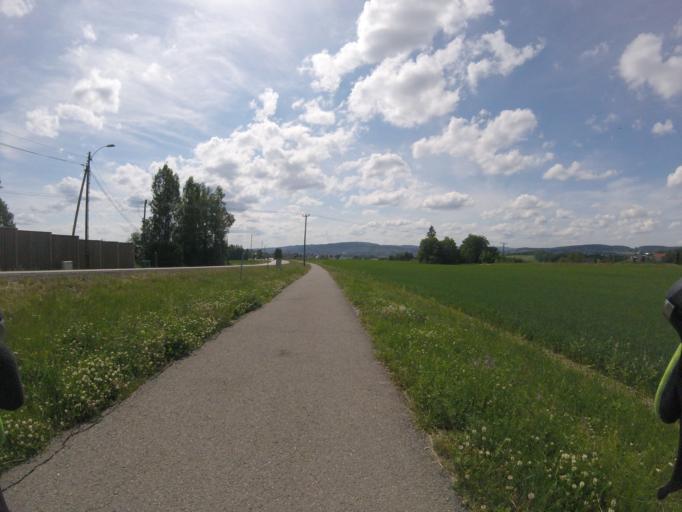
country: NO
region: Akershus
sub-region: Skedsmo
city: Lillestrom
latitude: 59.9878
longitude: 11.0477
